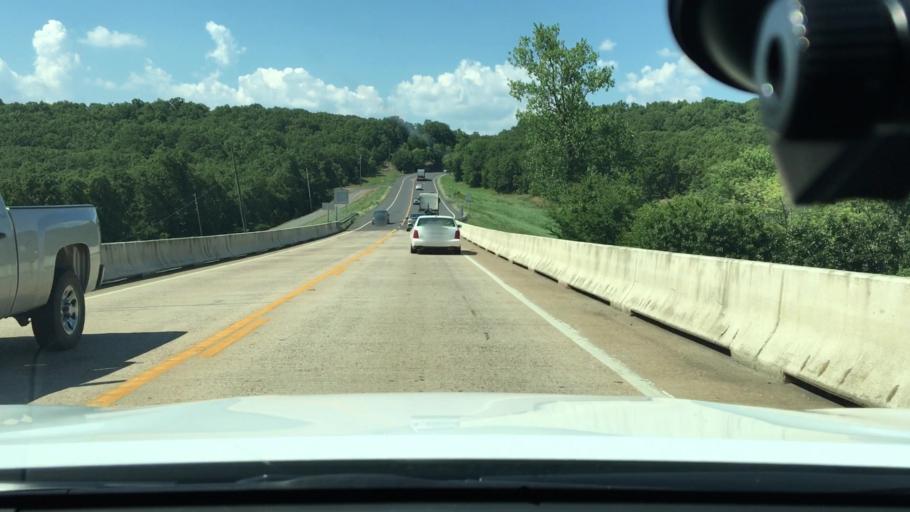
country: US
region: Arkansas
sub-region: Johnson County
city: Clarksville
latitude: 35.4131
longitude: -93.5322
